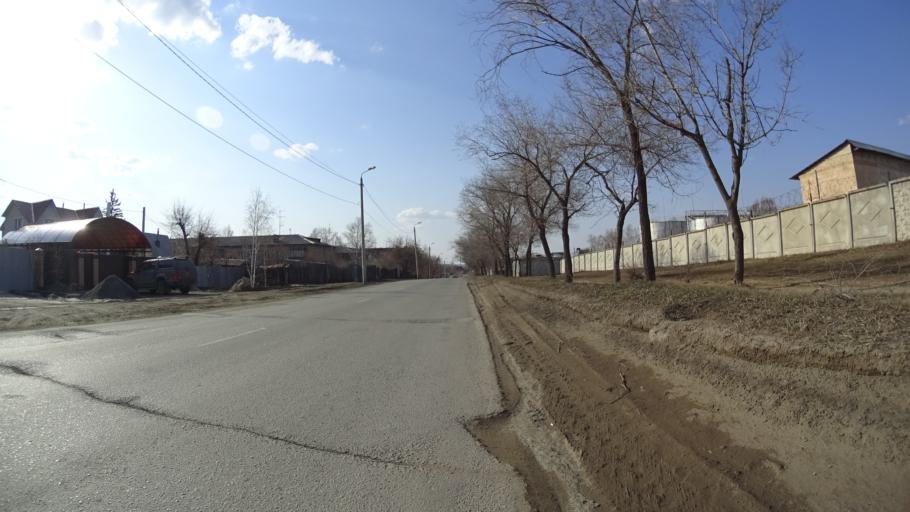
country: RU
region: Chelyabinsk
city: Novosineglazovskiy
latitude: 55.1051
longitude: 61.3401
